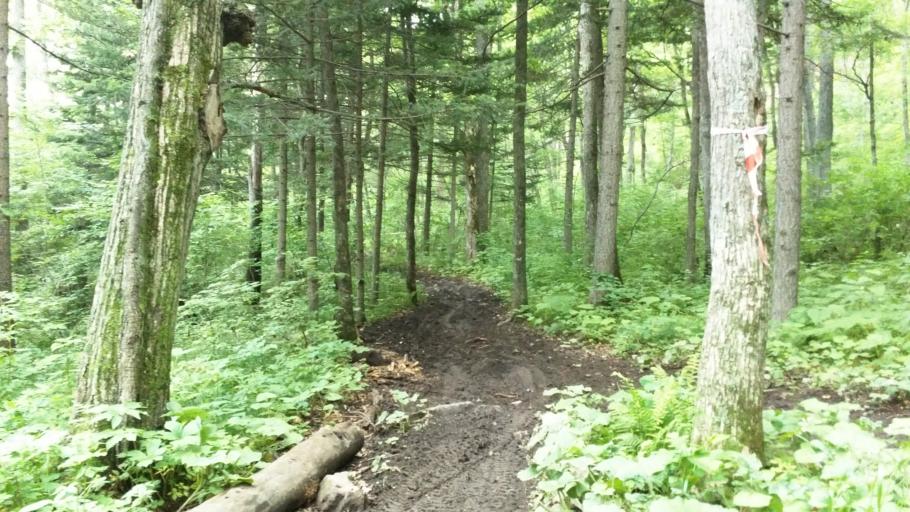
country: RU
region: Primorskiy
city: Trudovoye
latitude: 43.2079
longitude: 132.0024
